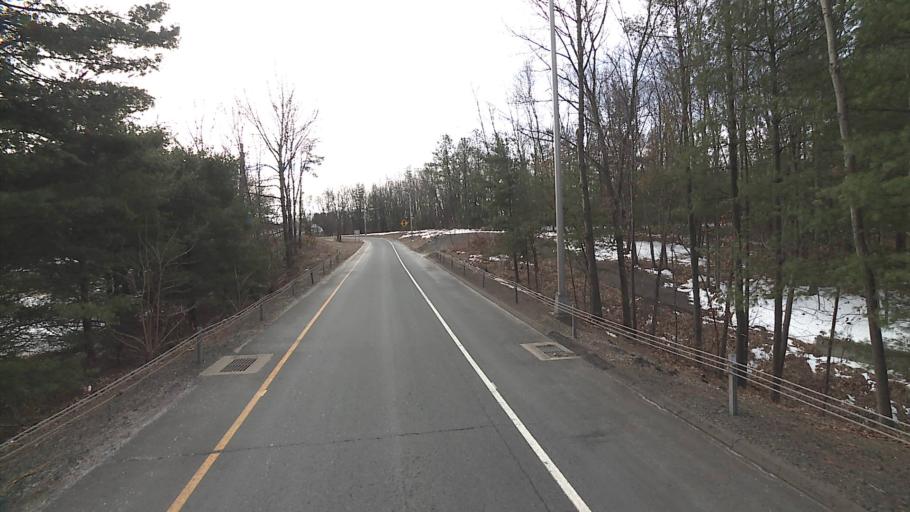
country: US
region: Connecticut
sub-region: Hartford County
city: Windsor Locks
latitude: 41.9165
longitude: -72.6778
